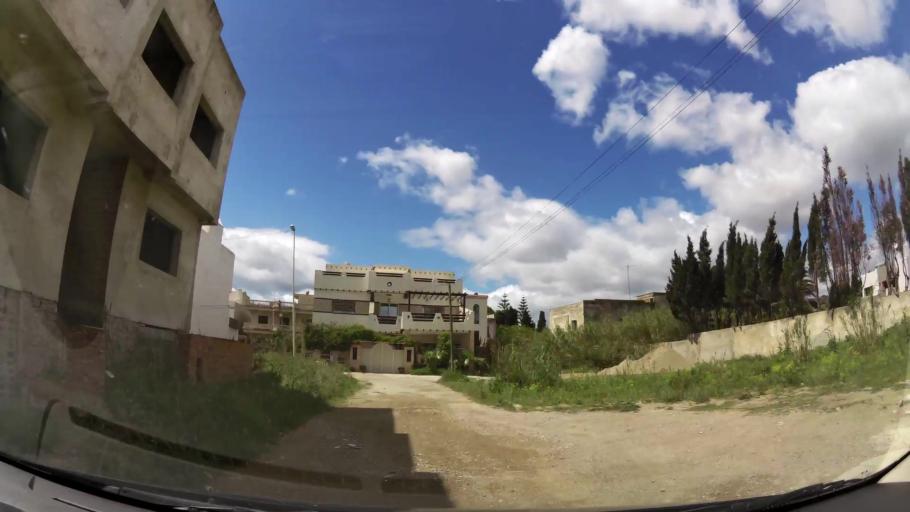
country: MA
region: Tanger-Tetouan
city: Tetouan
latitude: 35.5799
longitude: -5.3360
